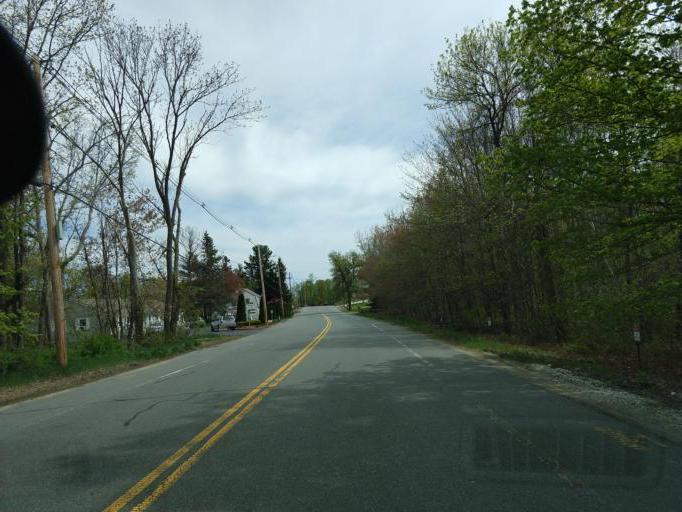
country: US
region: Massachusetts
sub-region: Essex County
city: Merrimac
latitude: 42.8250
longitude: -71.0183
